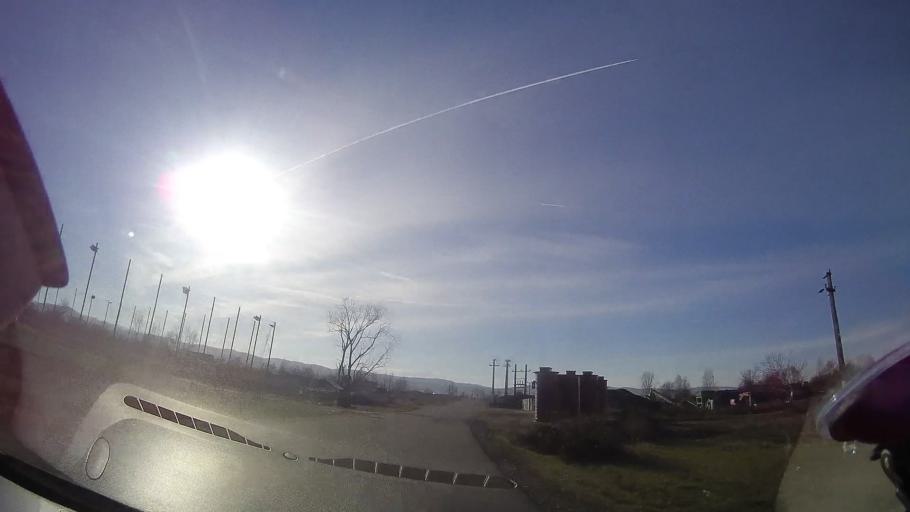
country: RO
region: Bihor
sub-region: Comuna Auseu
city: Auseu
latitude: 47.0289
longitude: 22.4924
